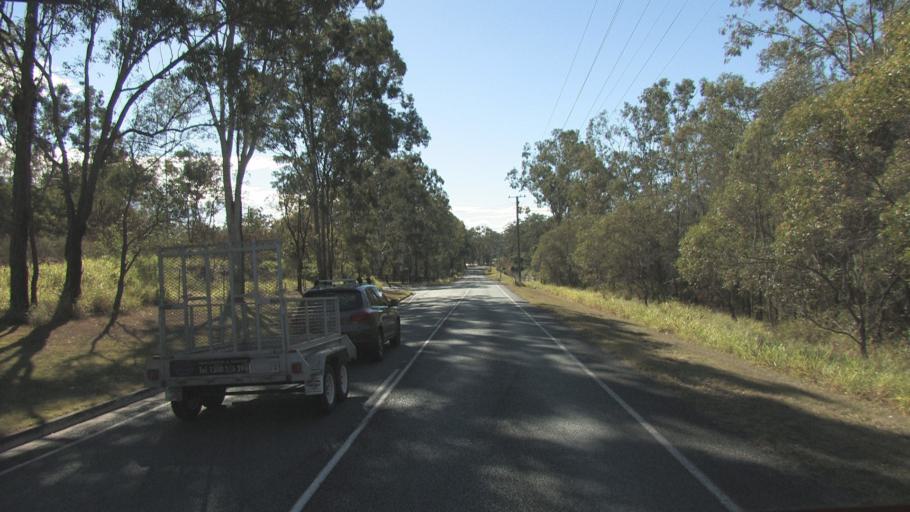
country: AU
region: Queensland
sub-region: Logan
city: North Maclean
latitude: -27.8194
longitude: 153.0566
